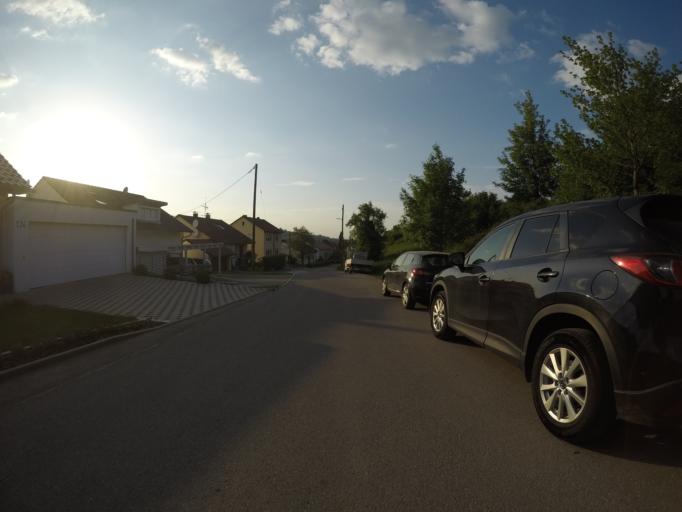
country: DE
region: Baden-Wuerttemberg
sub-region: Tuebingen Region
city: Pfullingen
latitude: 48.4571
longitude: 9.2342
